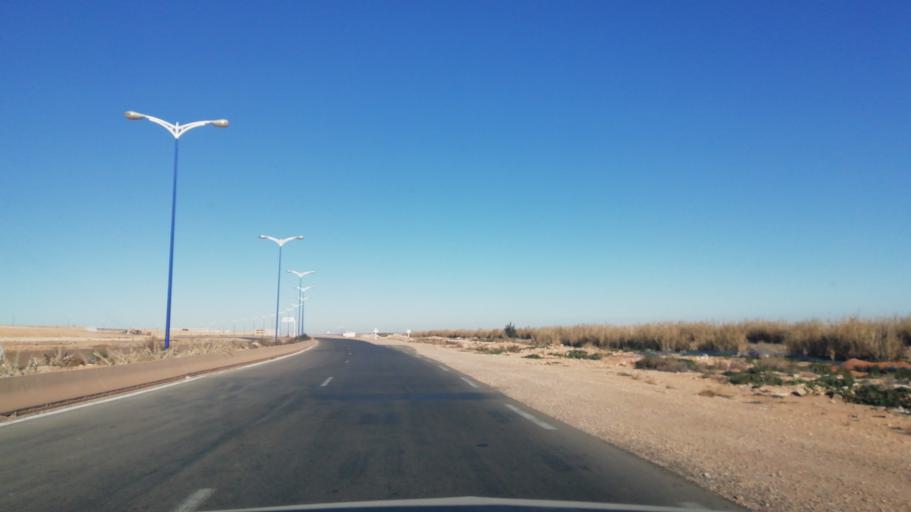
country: DZ
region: Wilaya de Naama
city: Naama
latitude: 33.5515
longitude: -0.2406
